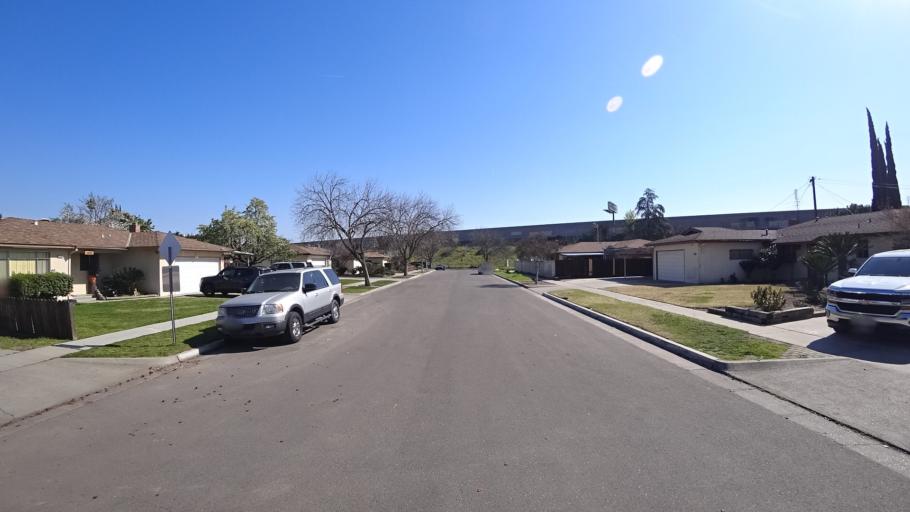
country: US
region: California
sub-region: Fresno County
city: Tarpey Village
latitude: 36.8031
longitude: -119.7402
